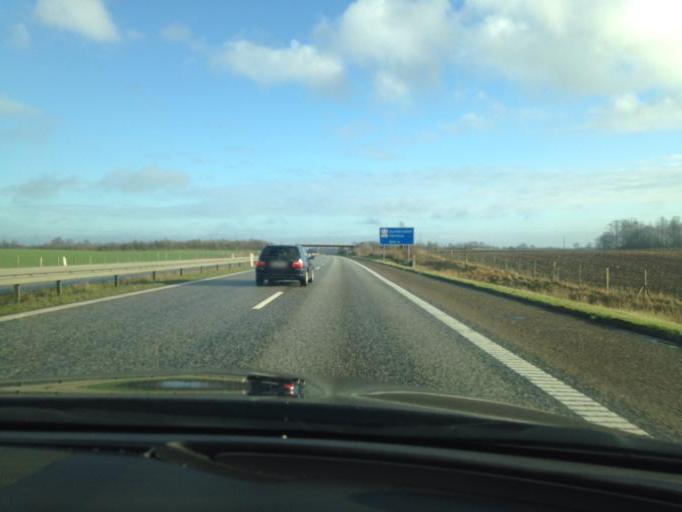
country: DK
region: South Denmark
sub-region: Kolding Kommune
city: Lunderskov
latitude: 55.5020
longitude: 9.2604
